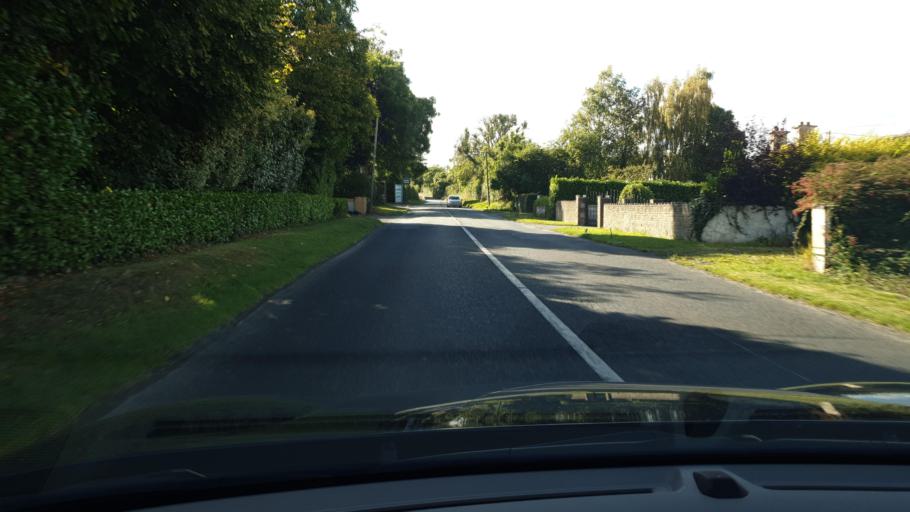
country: IE
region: Leinster
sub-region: An Mhi
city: Ashbourne
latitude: 53.4978
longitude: -6.4199
